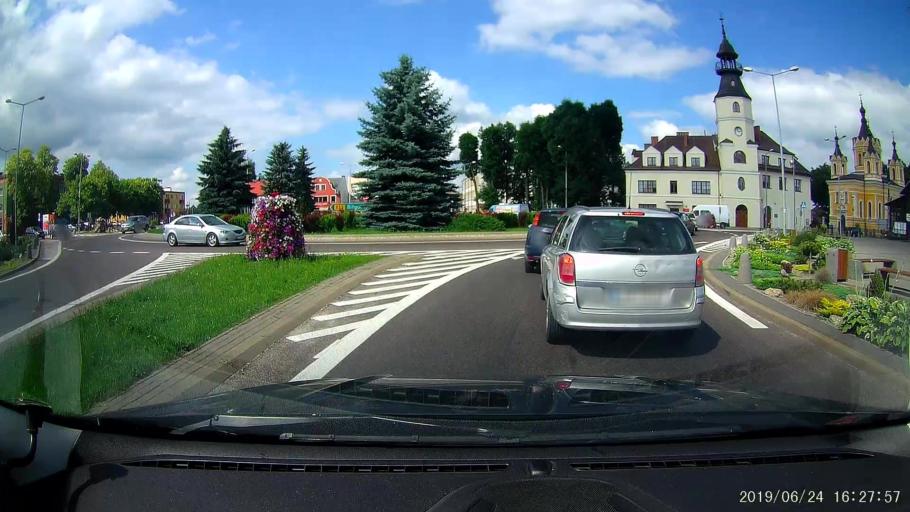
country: PL
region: Lublin Voivodeship
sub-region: Powiat tomaszowski
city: Tomaszow Lubelski
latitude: 50.4529
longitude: 23.4191
